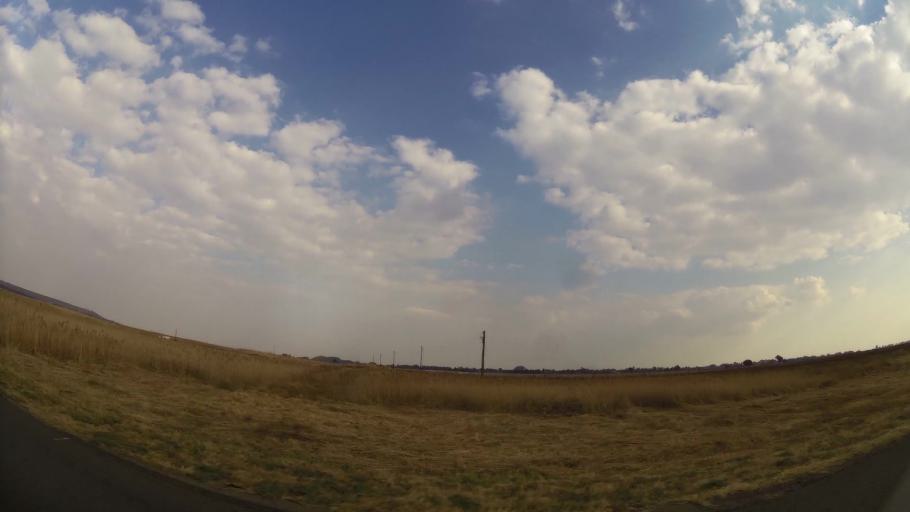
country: ZA
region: Gauteng
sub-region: Ekurhuleni Metropolitan Municipality
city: Springs
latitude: -26.2702
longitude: 28.4988
